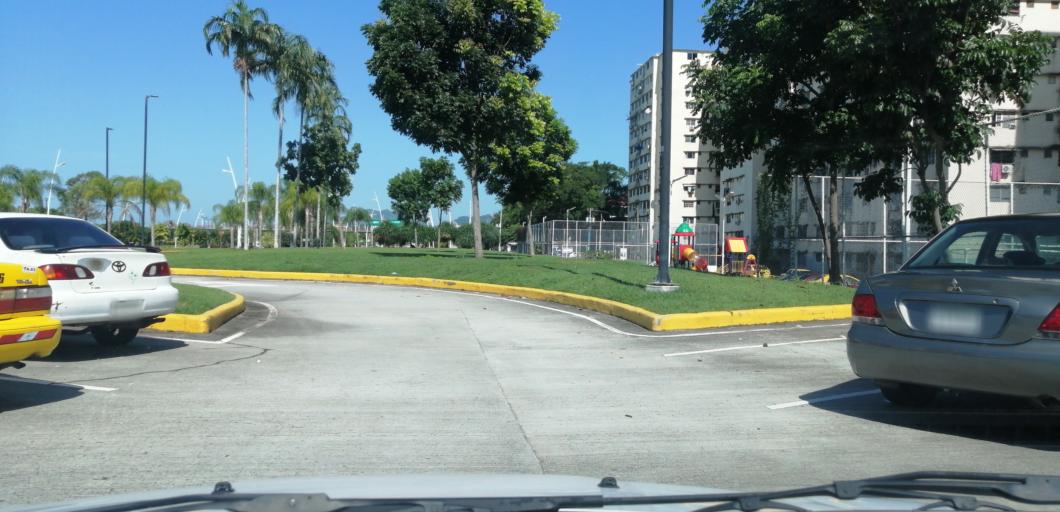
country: PA
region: Panama
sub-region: Distrito de Panama
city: Ancon
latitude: 8.9498
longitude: -79.5398
